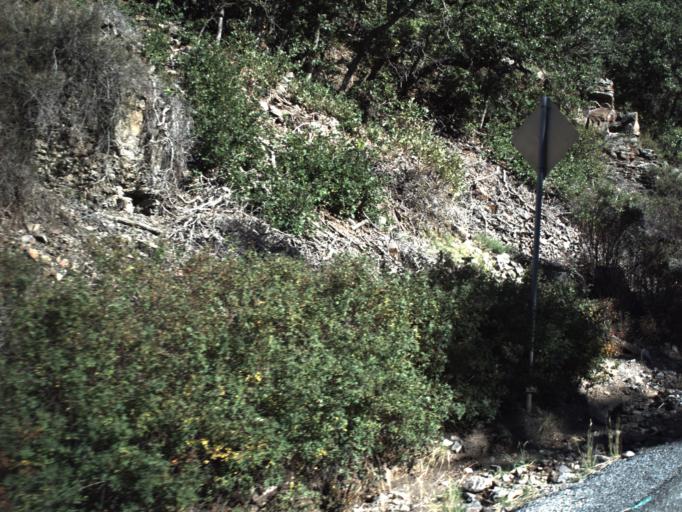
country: US
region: Utah
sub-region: Iron County
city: Parowan
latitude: 37.7615
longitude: -112.8499
